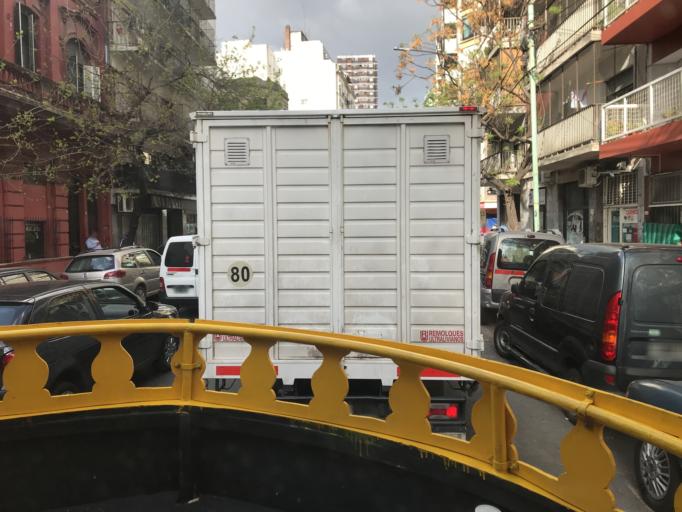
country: AR
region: Buenos Aires F.D.
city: Buenos Aires
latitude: -34.6054
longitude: -58.4074
